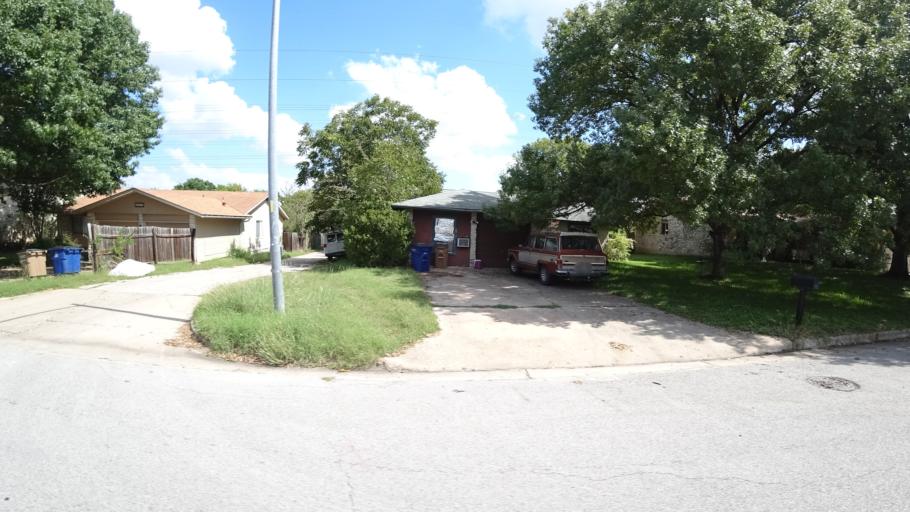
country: US
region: Texas
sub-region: Travis County
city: Onion Creek
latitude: 30.1935
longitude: -97.7835
